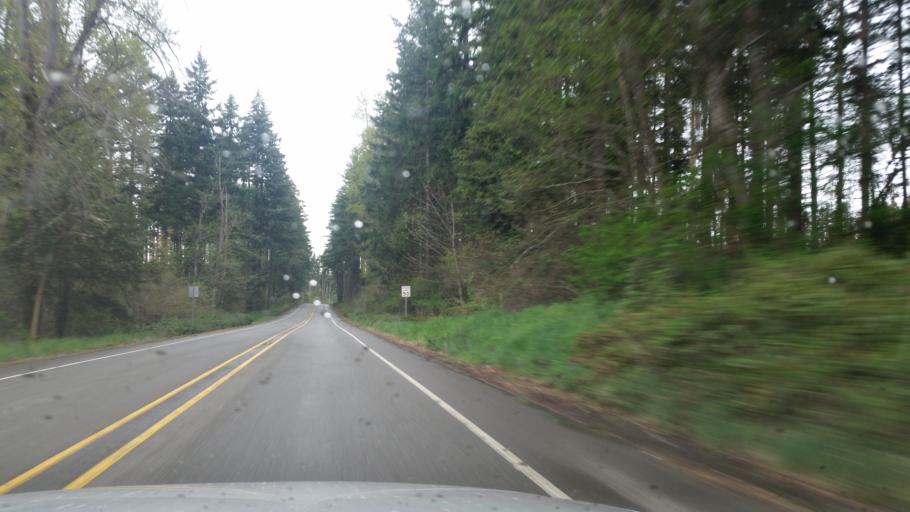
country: US
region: Washington
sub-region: Pierce County
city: Eatonville
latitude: 46.8361
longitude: -122.3199
